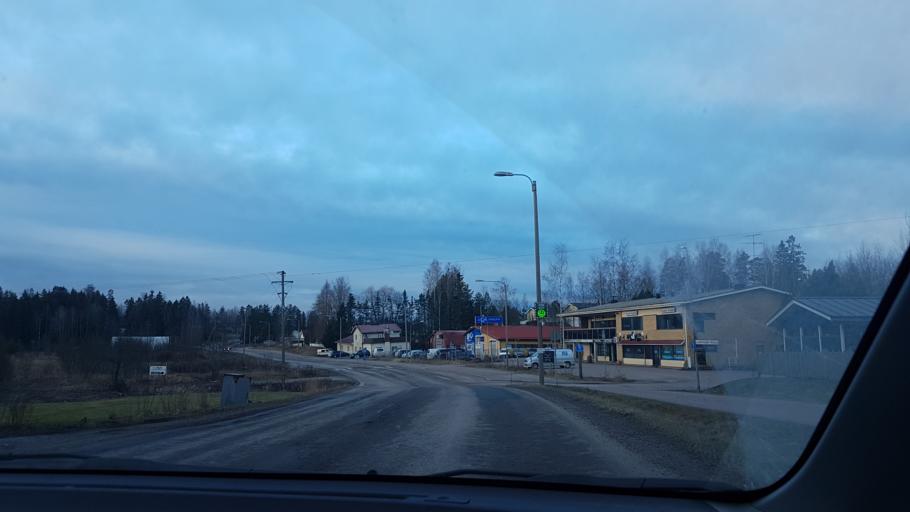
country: FI
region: Uusimaa
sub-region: Helsinki
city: Nurmijaervi
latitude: 60.3693
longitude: 24.7539
